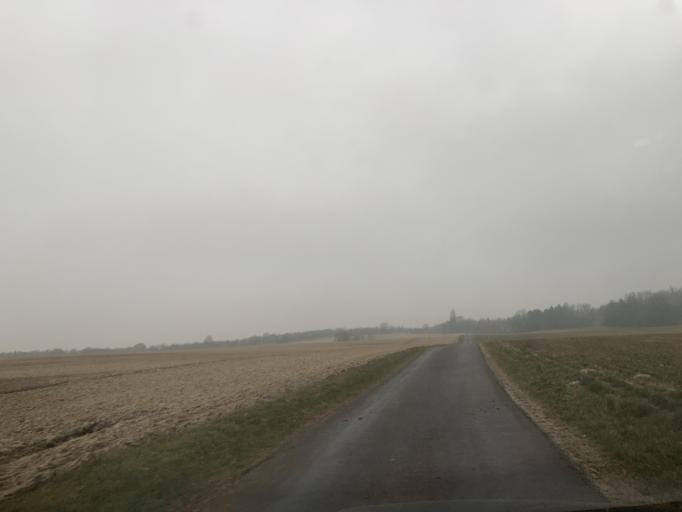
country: DK
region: Zealand
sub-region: Vordingborg Kommune
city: Neder Vindinge
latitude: 55.1557
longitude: 11.9019
